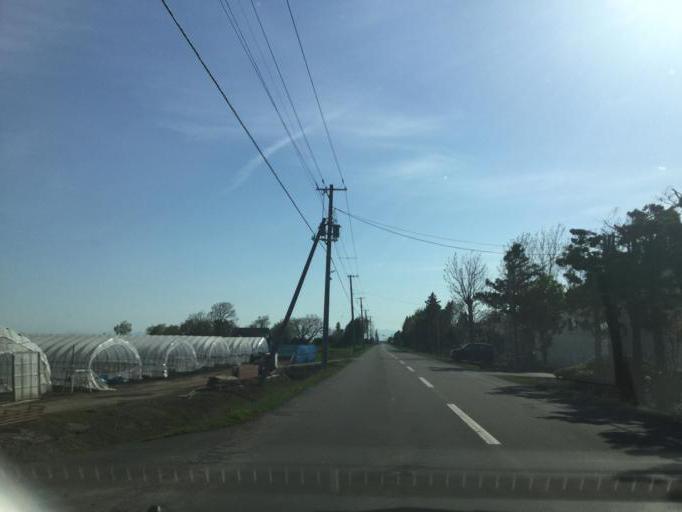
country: JP
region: Hokkaido
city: Iwamizawa
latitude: 43.1688
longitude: 141.7385
